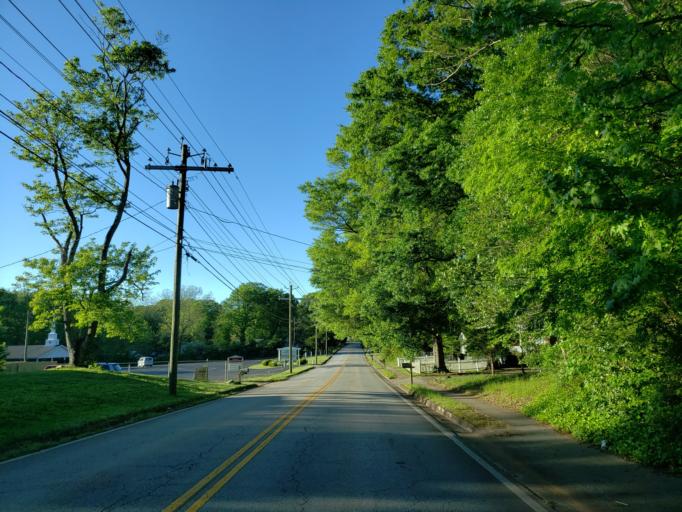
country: US
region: Georgia
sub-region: Cobb County
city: Fair Oaks
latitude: 33.9128
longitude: -84.5399
